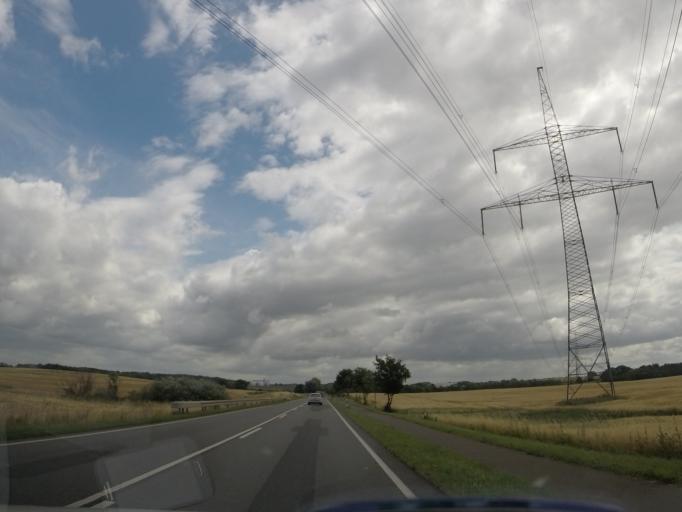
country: DE
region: Mecklenburg-Vorpommern
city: Lalendorf
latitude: 53.7621
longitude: 12.3636
